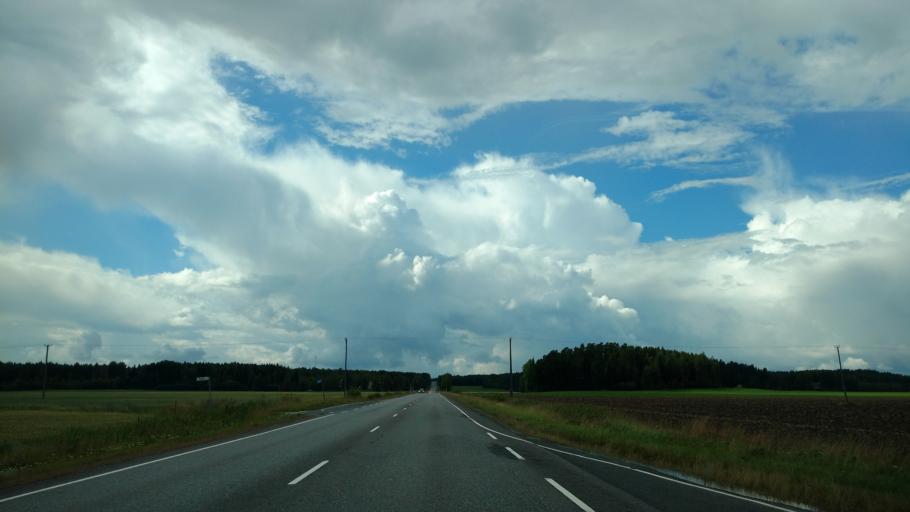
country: FI
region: Varsinais-Suomi
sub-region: Turku
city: Sauvo
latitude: 60.3937
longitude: 22.8596
